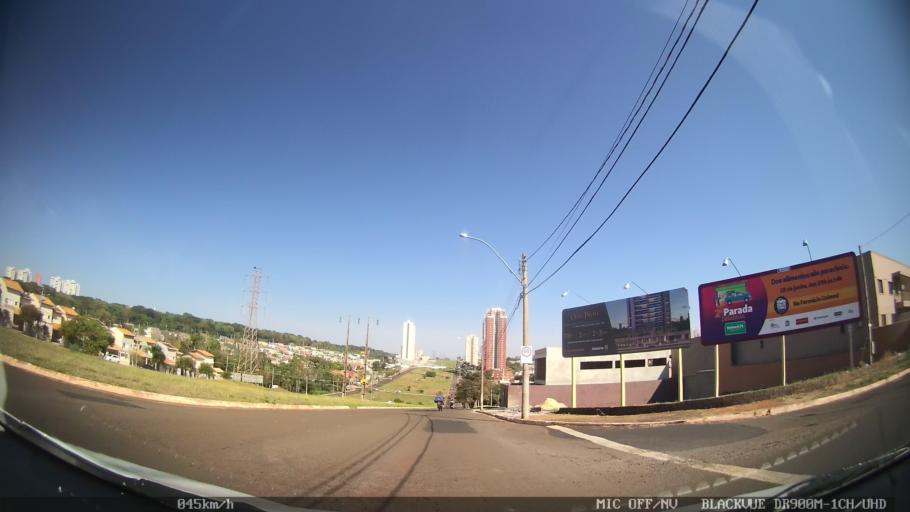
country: BR
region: Sao Paulo
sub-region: Ribeirao Preto
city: Ribeirao Preto
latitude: -21.2173
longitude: -47.7898
